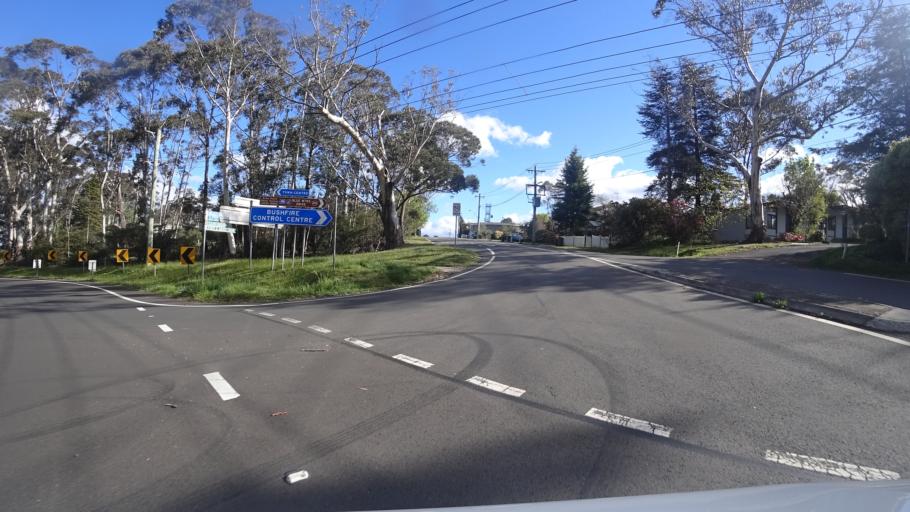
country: AU
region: New South Wales
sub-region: Blue Mountains Municipality
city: Katoomba
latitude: -33.7085
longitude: 150.3007
